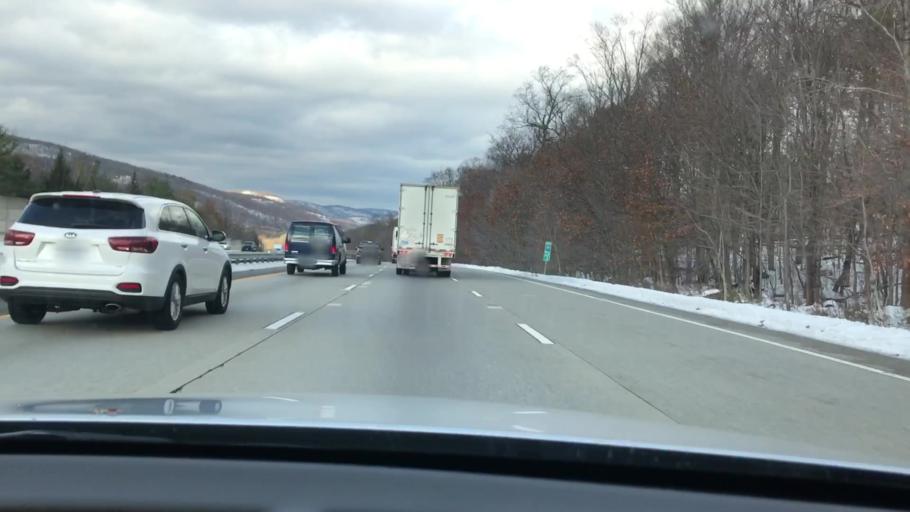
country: US
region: New Jersey
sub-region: Bergen County
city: Mahwah
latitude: 41.0832
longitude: -74.1688
